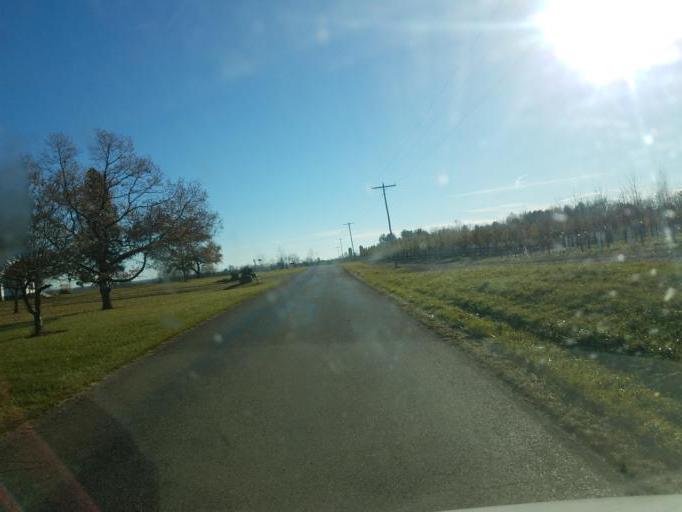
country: US
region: Ohio
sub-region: Knox County
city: Fredericktown
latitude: 40.4568
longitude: -82.5954
